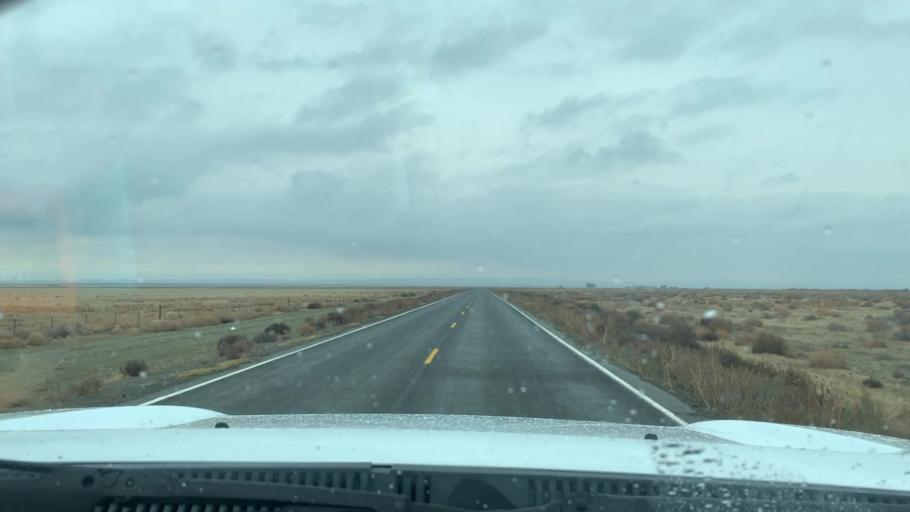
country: US
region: California
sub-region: Kings County
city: Kettleman City
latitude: 35.9341
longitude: -119.7822
